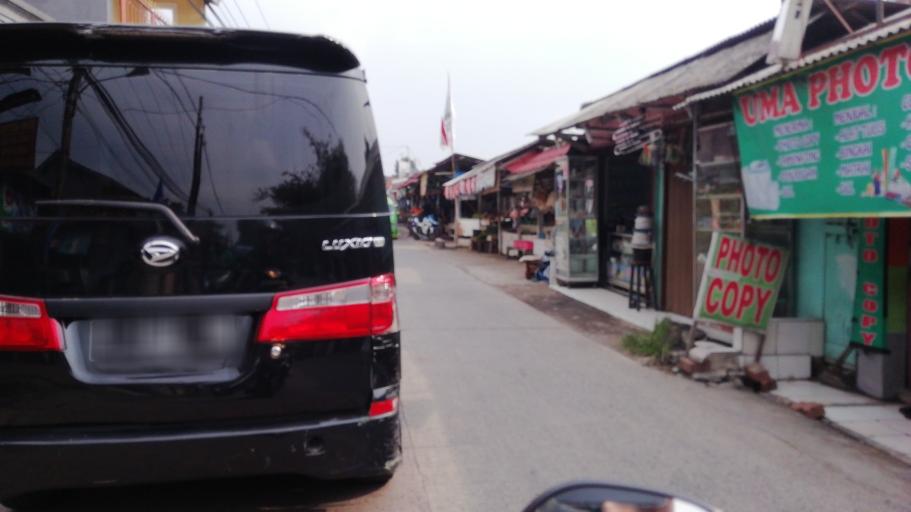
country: ID
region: West Java
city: Bogor
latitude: -6.5511
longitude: 106.7994
